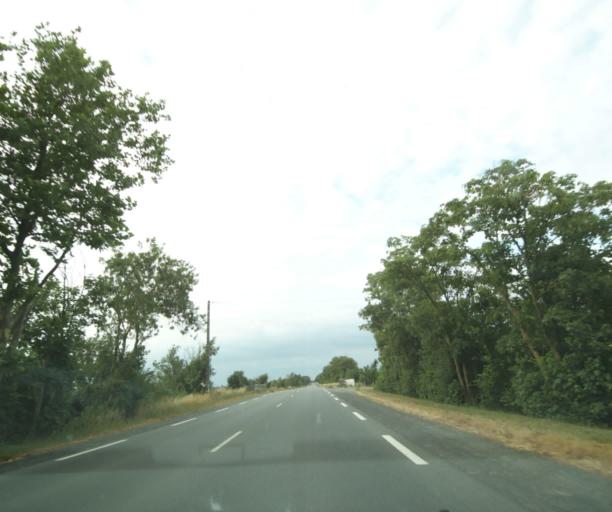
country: FR
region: Poitou-Charentes
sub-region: Departement de la Charente-Maritime
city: Marans
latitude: 46.2893
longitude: -0.9927
